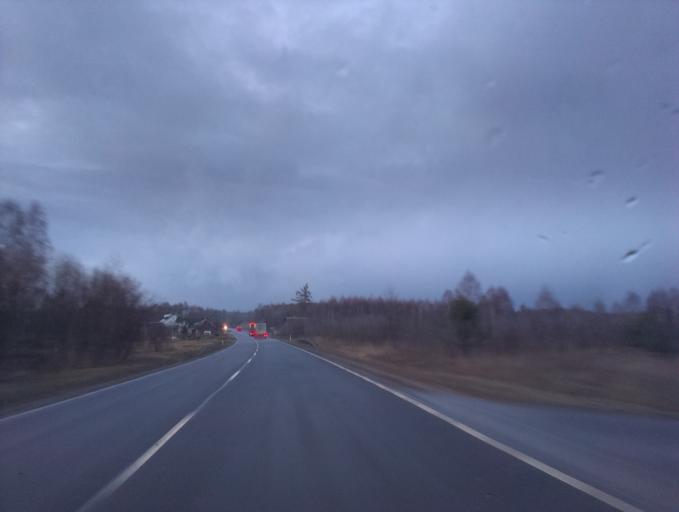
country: PL
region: Lodz Voivodeship
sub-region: Powiat opoczynski
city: Zarnow
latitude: 51.2222
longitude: 20.1853
